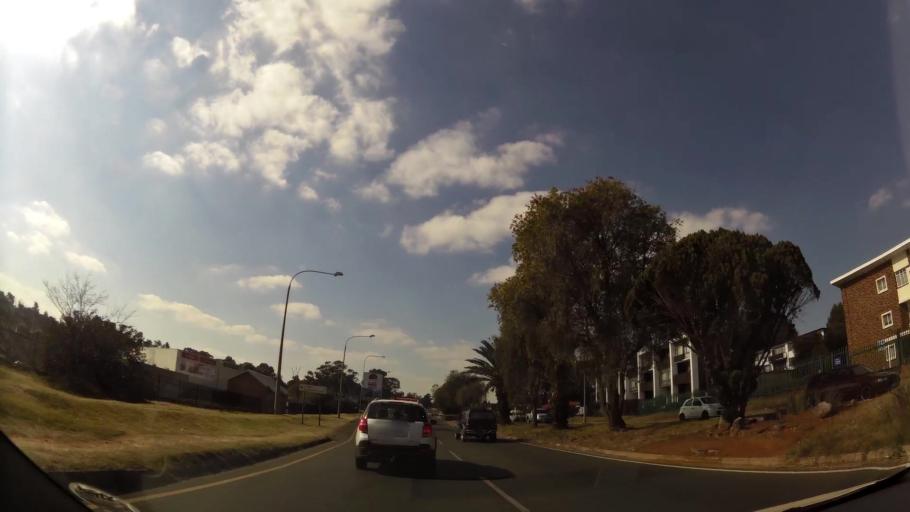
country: ZA
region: Gauteng
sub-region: West Rand District Municipality
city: Krugersdorp
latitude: -26.0887
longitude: 27.7834
